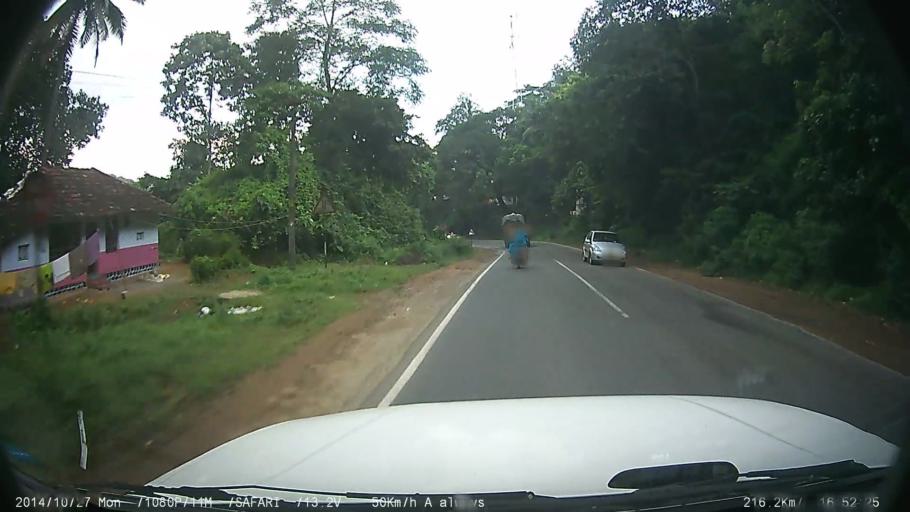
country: IN
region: Kerala
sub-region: Thrissur District
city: Chelakara
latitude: 10.5740
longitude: 76.3850
